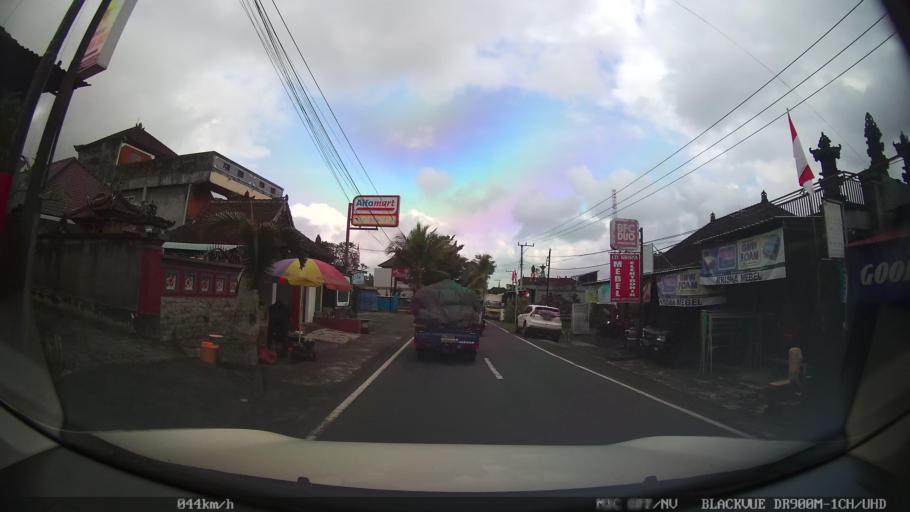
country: ID
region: Bali
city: Pohgending Kawan
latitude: -8.4341
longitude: 115.1430
